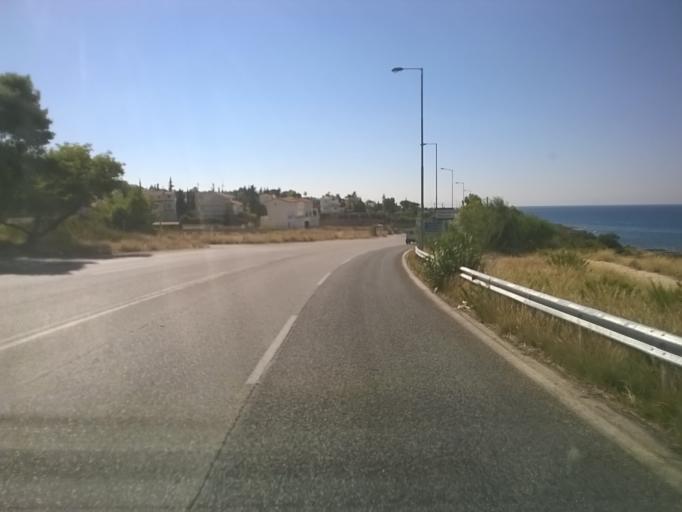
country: GR
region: Attica
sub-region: Nomarchia Anatolikis Attikis
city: Saronida
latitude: 37.7694
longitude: 23.9027
